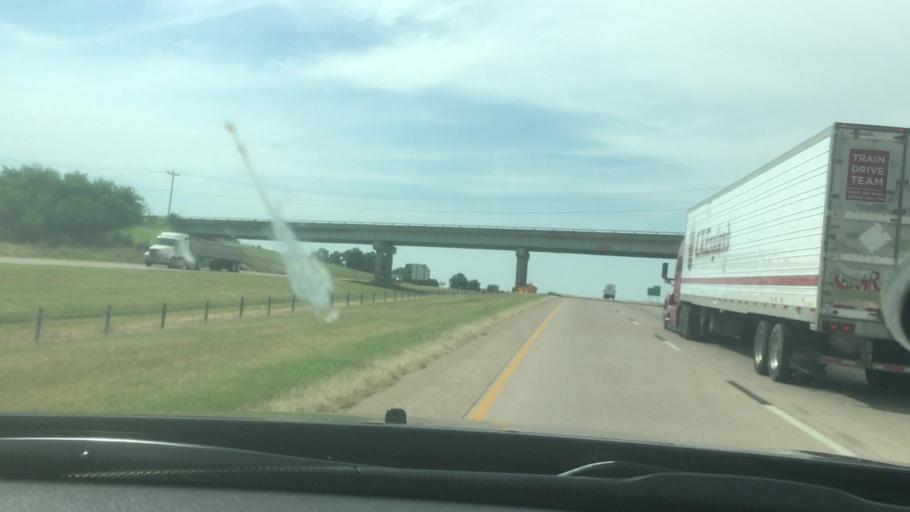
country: US
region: Oklahoma
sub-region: Garvin County
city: Pauls Valley
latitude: 34.7256
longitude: -97.2545
